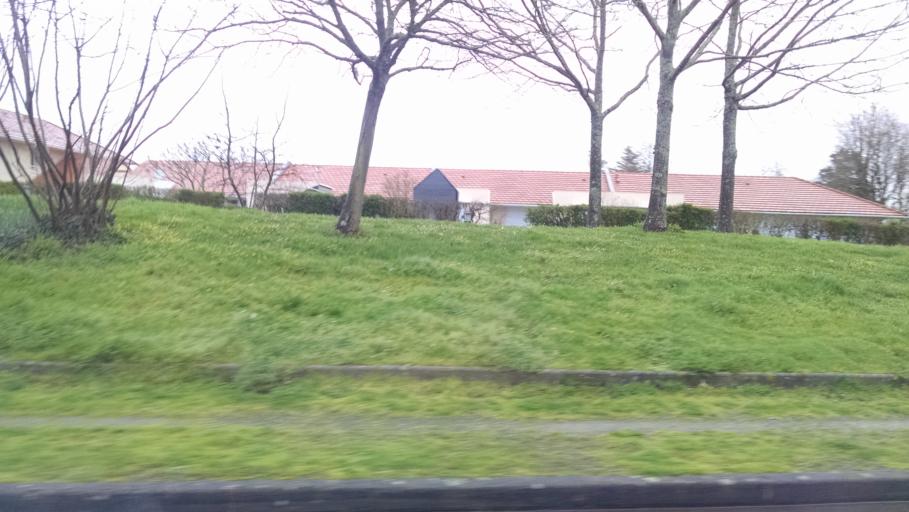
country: FR
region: Pays de la Loire
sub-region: Departement de la Loire-Atlantique
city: Aigrefeuille-sur-Maine
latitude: 47.0809
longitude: -1.4021
